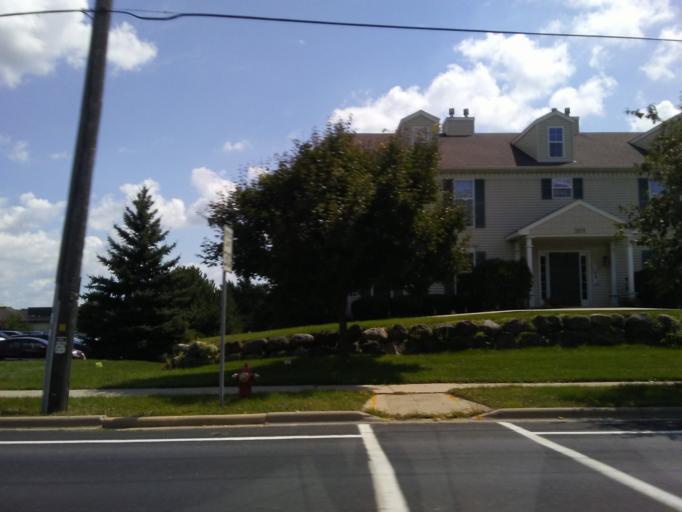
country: US
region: Wisconsin
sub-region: Dane County
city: Verona
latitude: 43.0106
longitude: -89.4990
